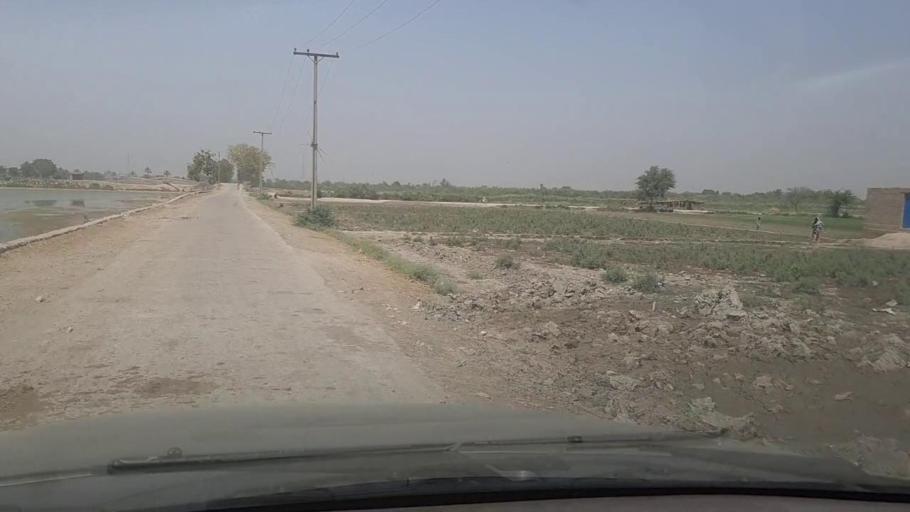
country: PK
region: Sindh
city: Madeji
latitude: 27.7981
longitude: 68.4203
